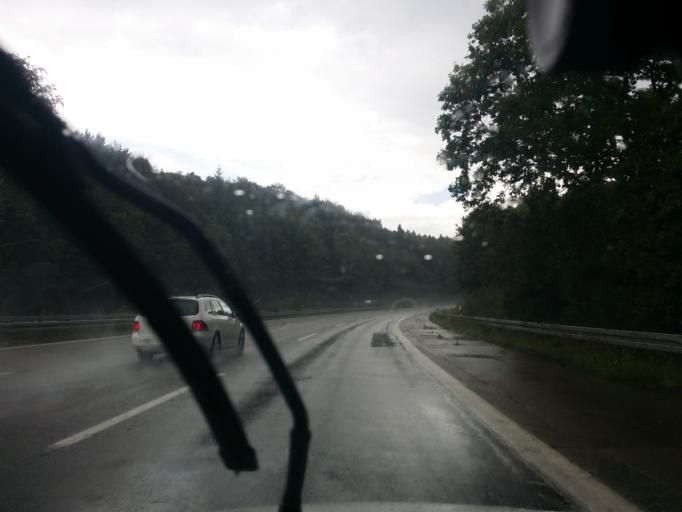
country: DE
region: Hesse
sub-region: Regierungsbezirk Kassel
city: Kirchheim
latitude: 50.8021
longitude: 9.5355
